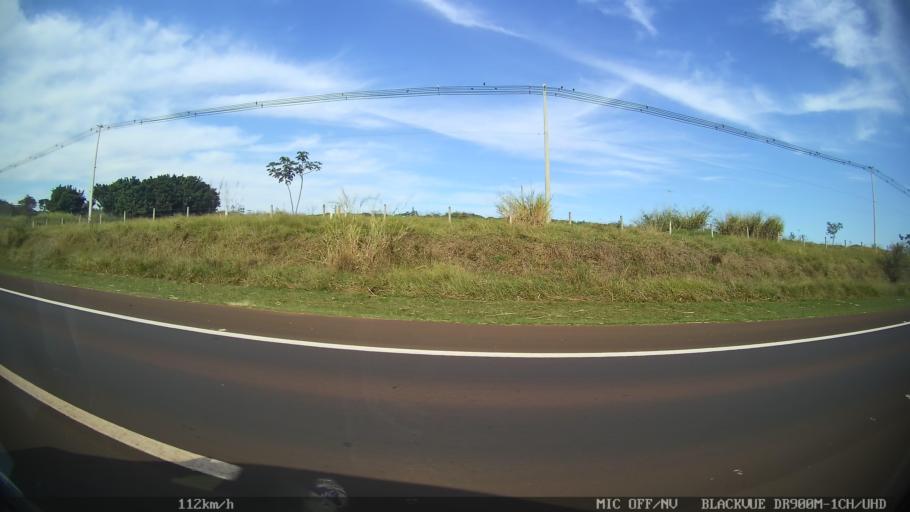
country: BR
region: Sao Paulo
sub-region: Americo Brasiliense
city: Americo Brasiliense
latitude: -21.7818
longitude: -48.1124
